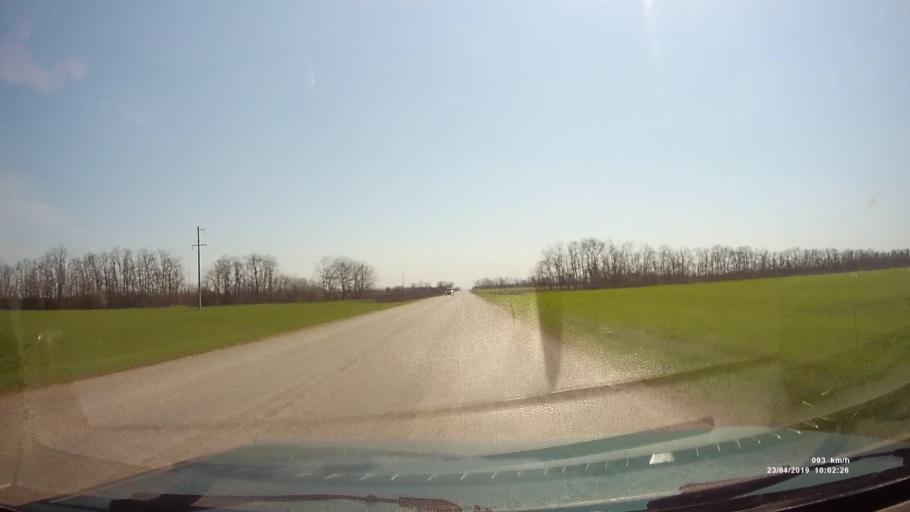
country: RU
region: Rostov
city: Sovetskoye
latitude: 46.7599
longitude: 42.1695
